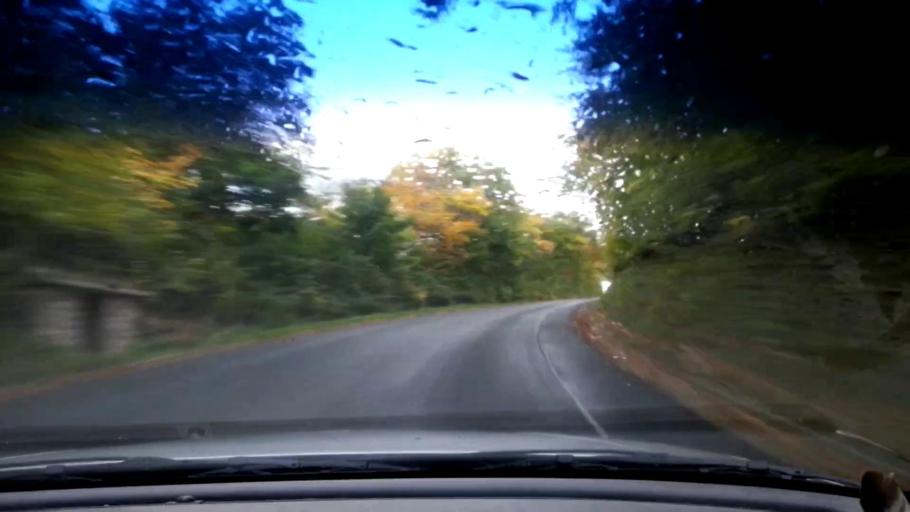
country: DE
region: Bavaria
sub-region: Upper Franconia
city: Priesendorf
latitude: 49.8589
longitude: 10.6883
